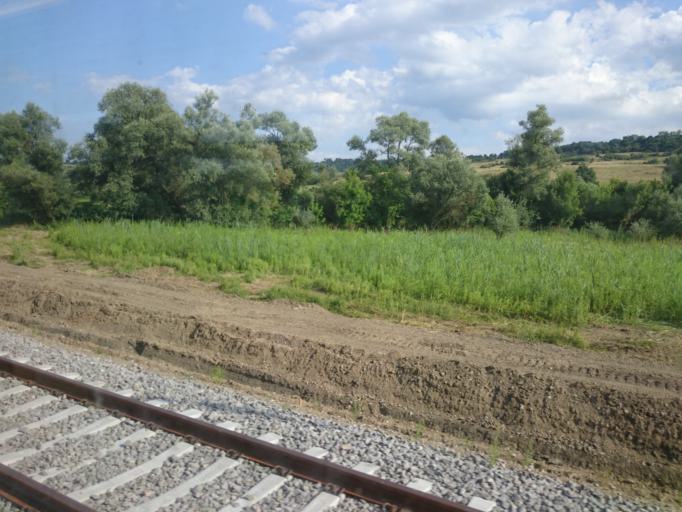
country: RO
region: Sibiu
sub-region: Comuna Laslea
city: Laslea
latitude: 46.2204
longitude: 24.6325
